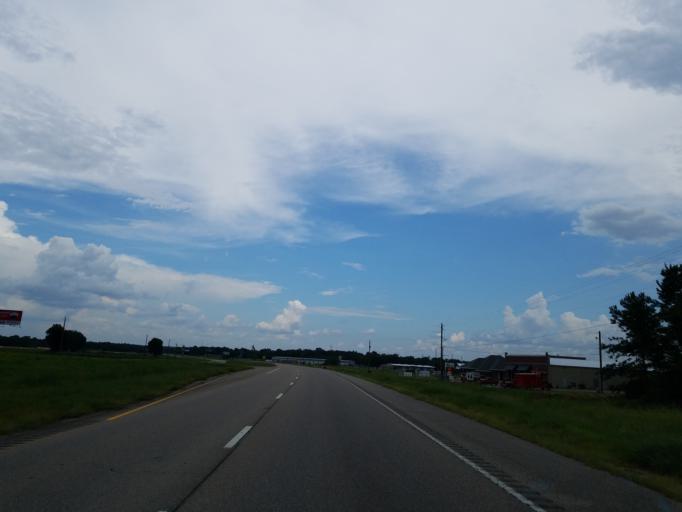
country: US
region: Mississippi
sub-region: Forrest County
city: Glendale
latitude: 31.3608
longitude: -89.2975
